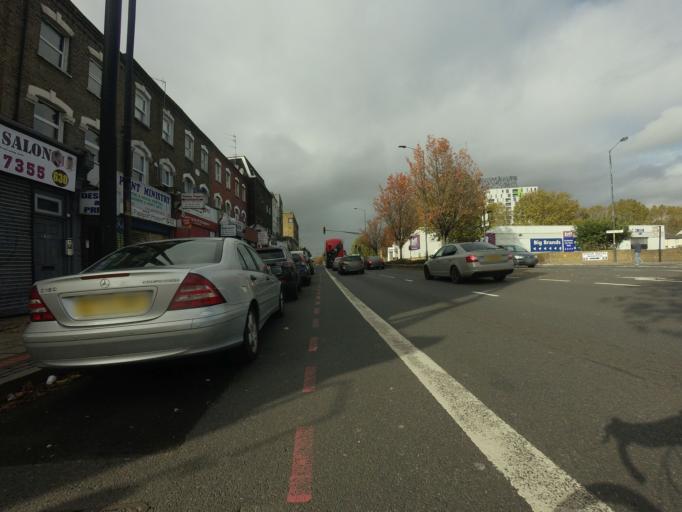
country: GB
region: England
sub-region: Greater London
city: Camberwell
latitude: 51.4830
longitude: -0.0642
